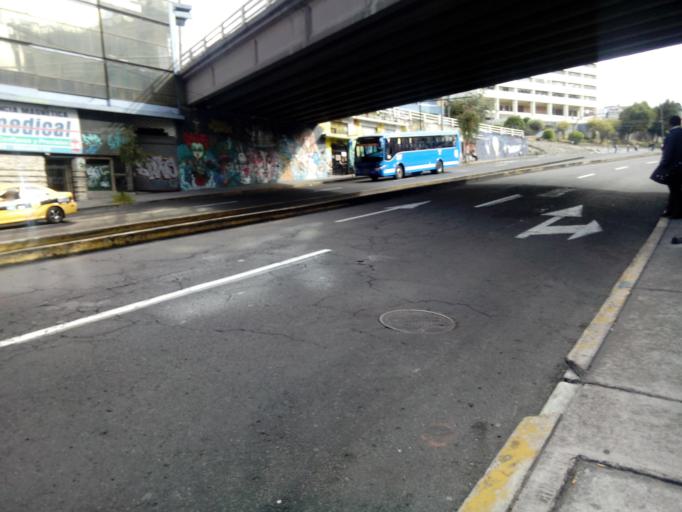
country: EC
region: Pichincha
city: Quito
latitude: -0.2132
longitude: -78.4972
